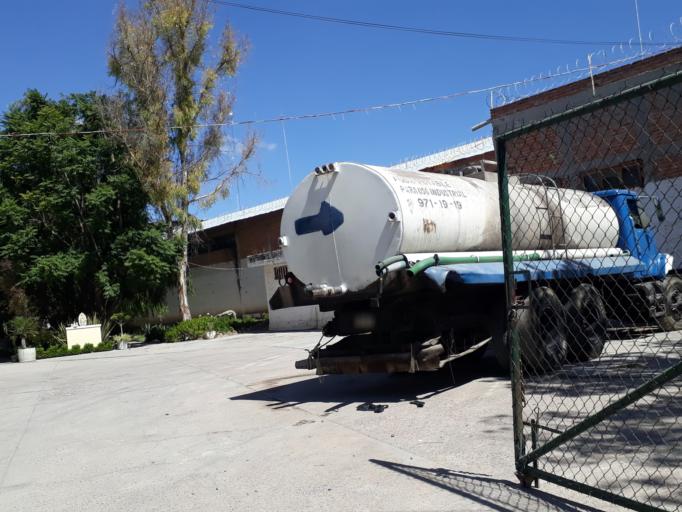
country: MX
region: Aguascalientes
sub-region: Aguascalientes
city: San Sebastian [Fraccionamiento]
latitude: 21.8061
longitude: -102.2893
